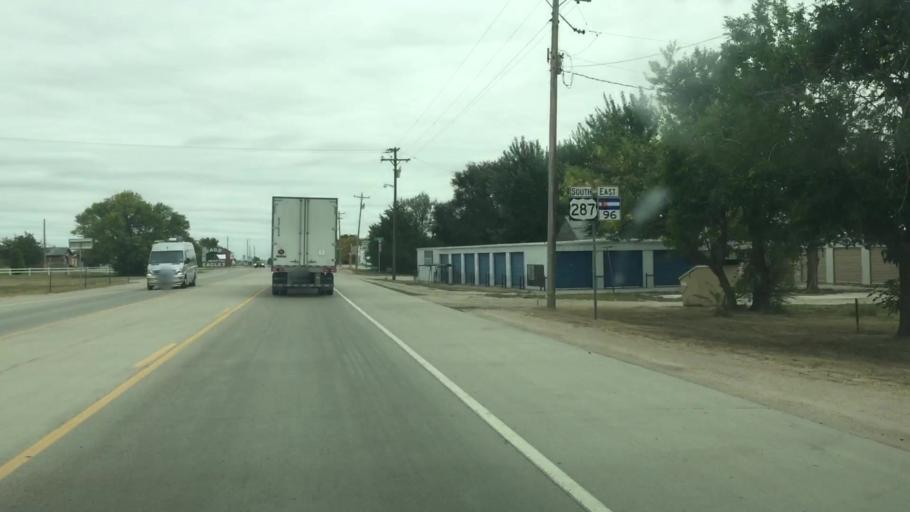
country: US
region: Colorado
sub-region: Kiowa County
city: Eads
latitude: 38.4778
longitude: -102.7813
